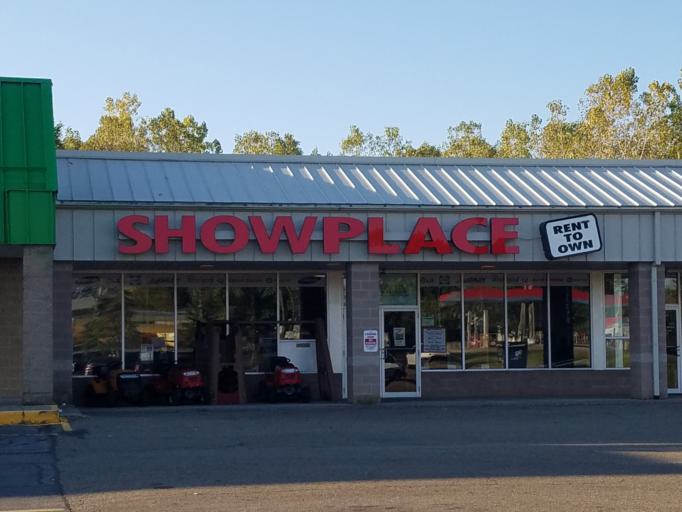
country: US
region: Ohio
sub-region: Morrow County
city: Mount Gilead
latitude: 40.5482
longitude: -82.8451
